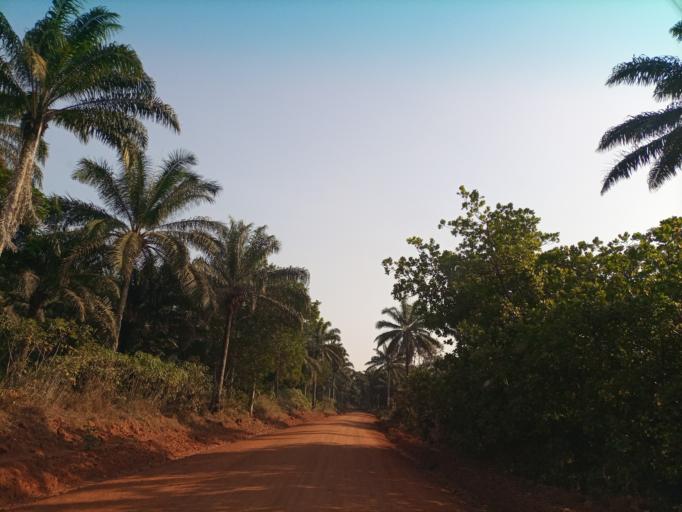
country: NG
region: Enugu
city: Opi
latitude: 6.7755
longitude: 7.3902
